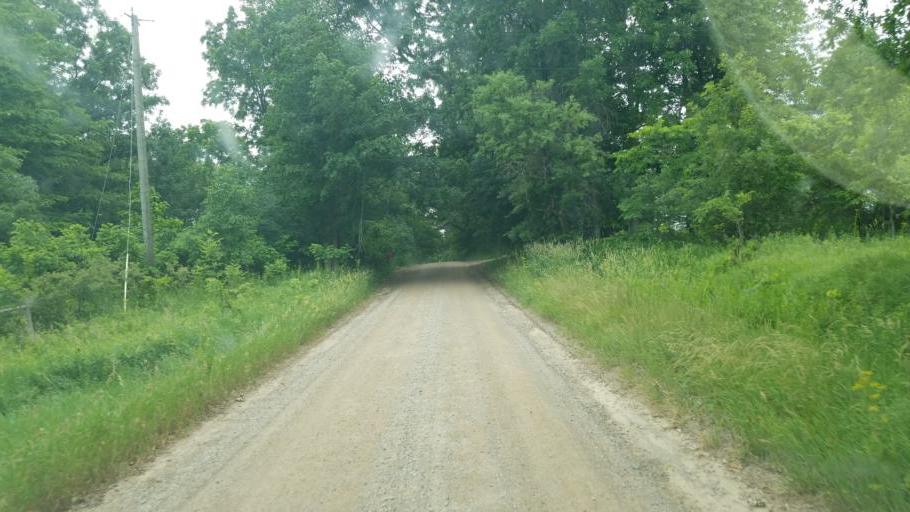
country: US
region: Michigan
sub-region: Barry County
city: Nashville
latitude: 42.6481
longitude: -84.9755
